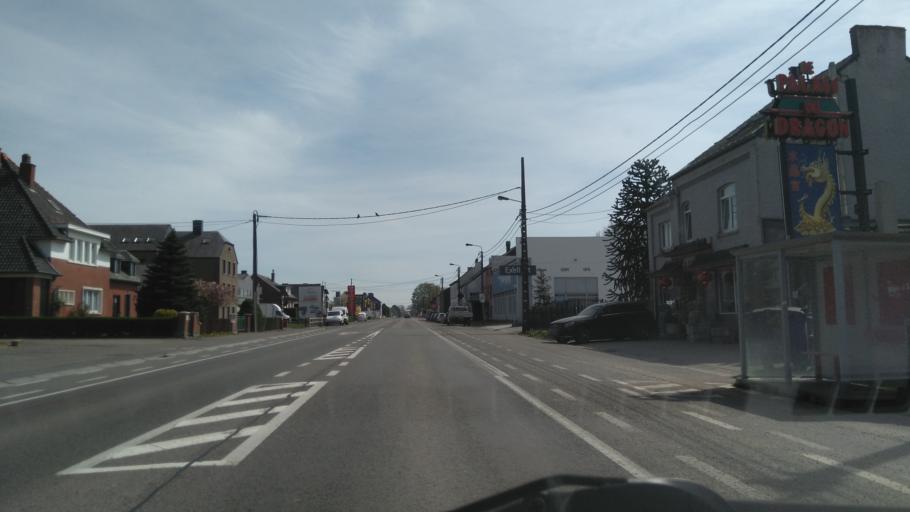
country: BE
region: Wallonia
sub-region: Province de Namur
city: Eghezee
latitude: 50.6002
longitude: 4.9029
